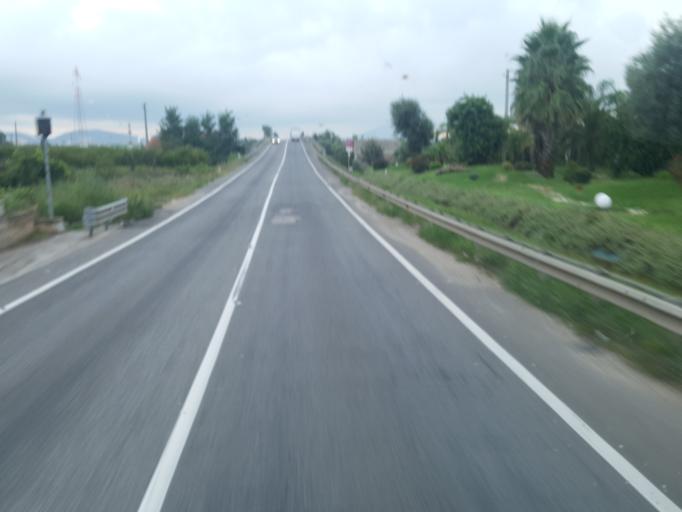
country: IT
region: Campania
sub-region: Provincia di Caserta
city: Sparanise
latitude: 41.1735
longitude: 14.1316
